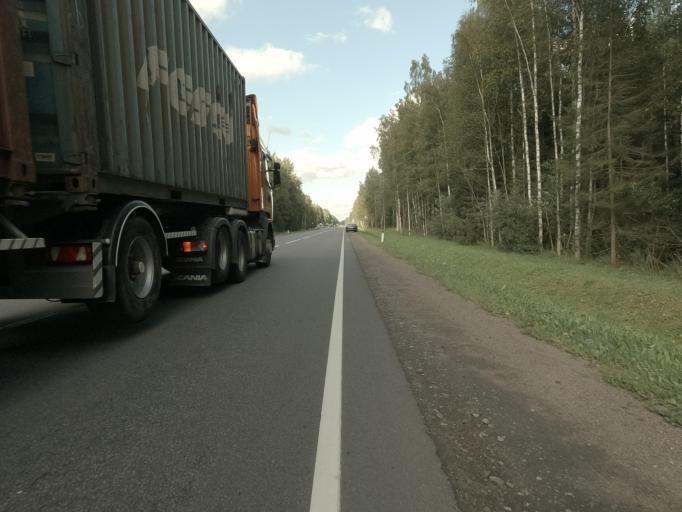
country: RU
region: Leningrad
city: Mga
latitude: 59.7048
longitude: 31.0093
